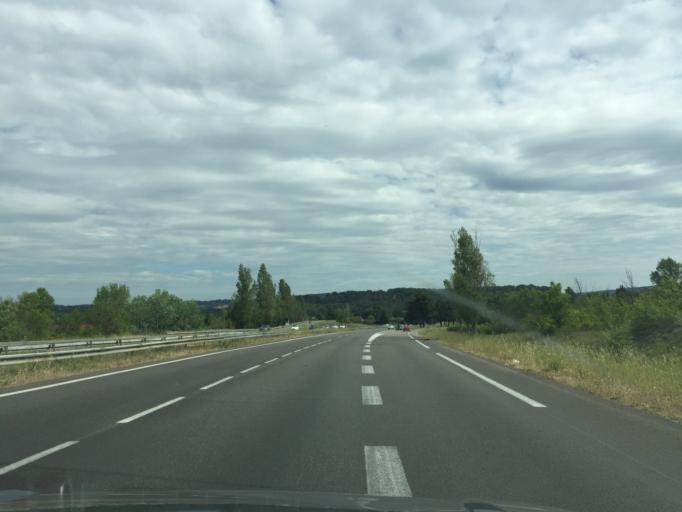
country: FR
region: Provence-Alpes-Cote d'Azur
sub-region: Departement des Bouches-du-Rhone
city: Aix-en-Provence
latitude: 43.5021
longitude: 5.4077
